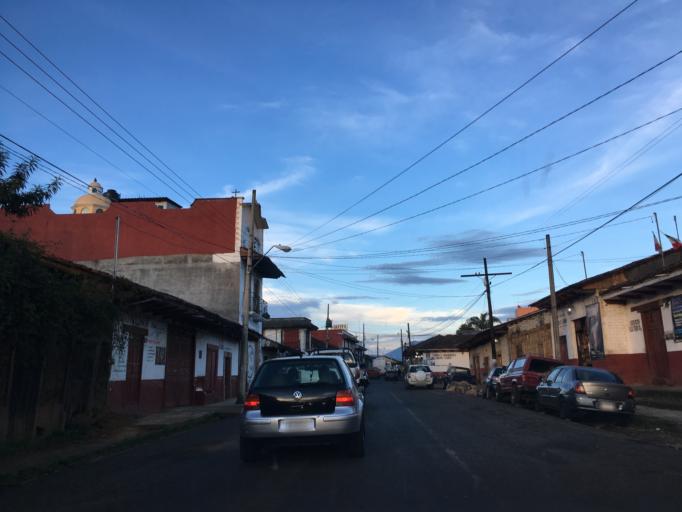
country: MX
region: Michoacan
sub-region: Salvador Escalante
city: Santa Clara del Cobre
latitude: 19.4046
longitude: -101.6434
